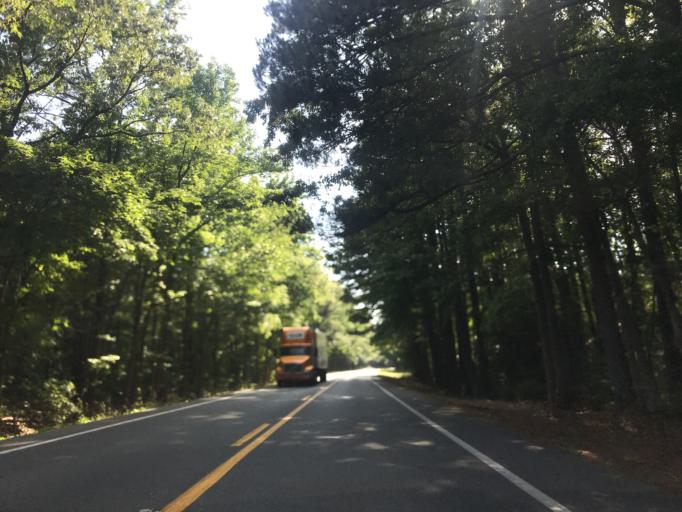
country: US
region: Maryland
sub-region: Wicomico County
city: Hebron
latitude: 38.4643
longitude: -75.7271
